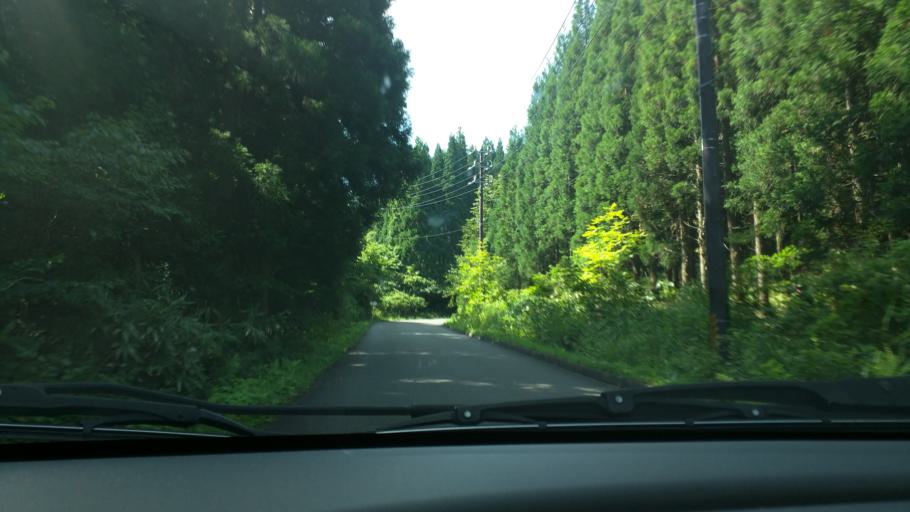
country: JP
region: Fukushima
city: Inawashiro
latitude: 37.3518
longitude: 140.0563
